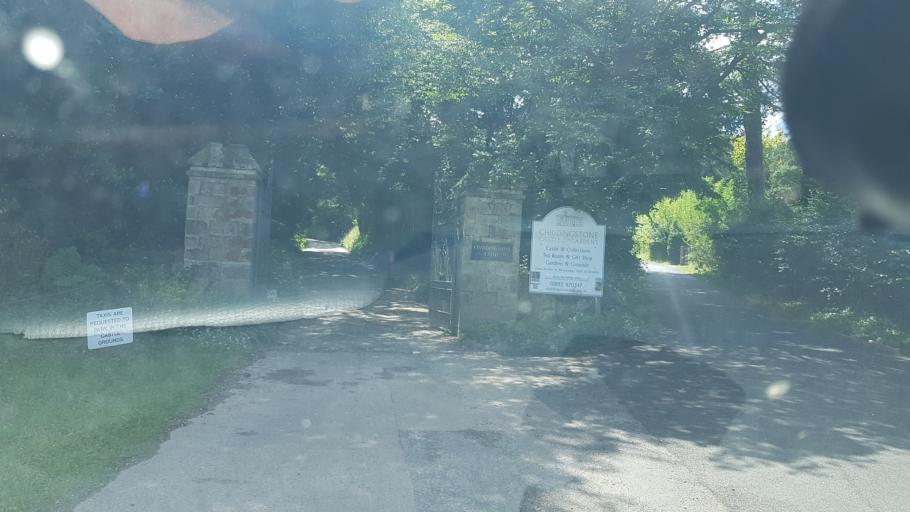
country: GB
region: England
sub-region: Kent
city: Edenbridge
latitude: 51.1876
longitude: 0.1410
